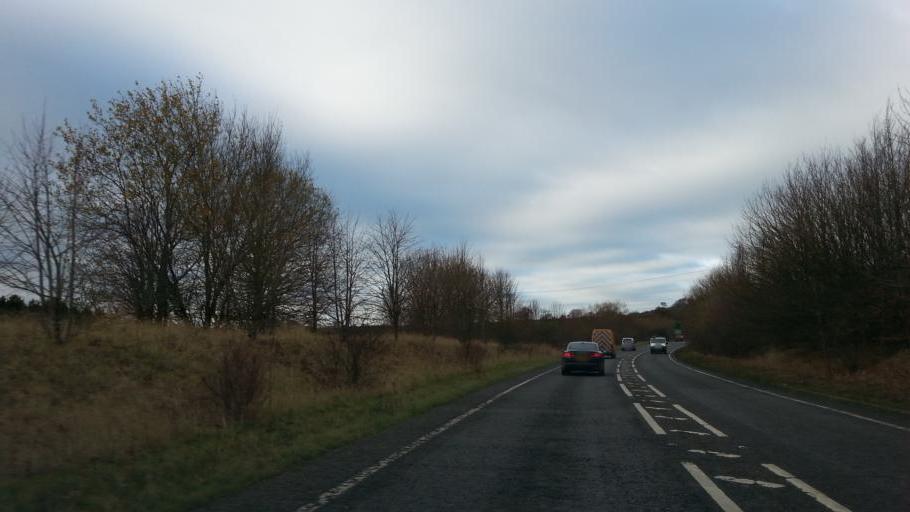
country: GB
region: England
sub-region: Suffolk
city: Botesdale
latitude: 52.3326
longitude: 0.9884
